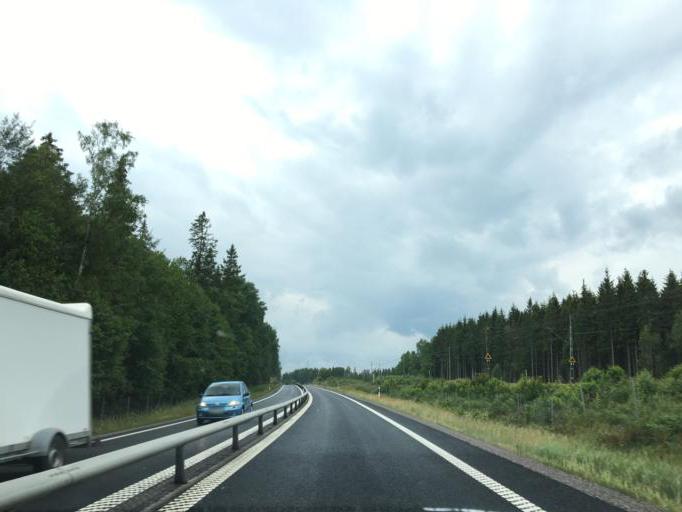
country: SE
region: Soedermanland
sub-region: Katrineholms Kommun
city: Katrineholm
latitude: 58.8752
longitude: 16.1984
